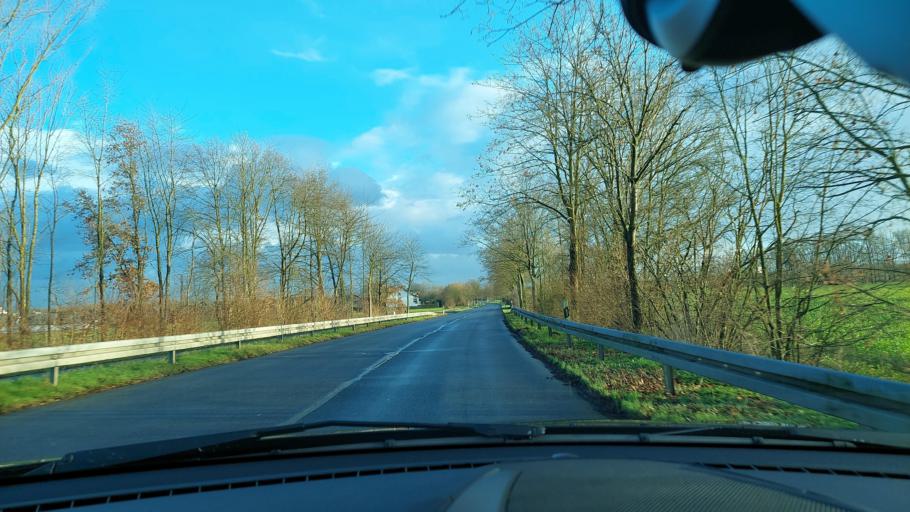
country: DE
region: North Rhine-Westphalia
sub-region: Regierungsbezirk Dusseldorf
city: Dormagen
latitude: 51.0714
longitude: 6.7989
